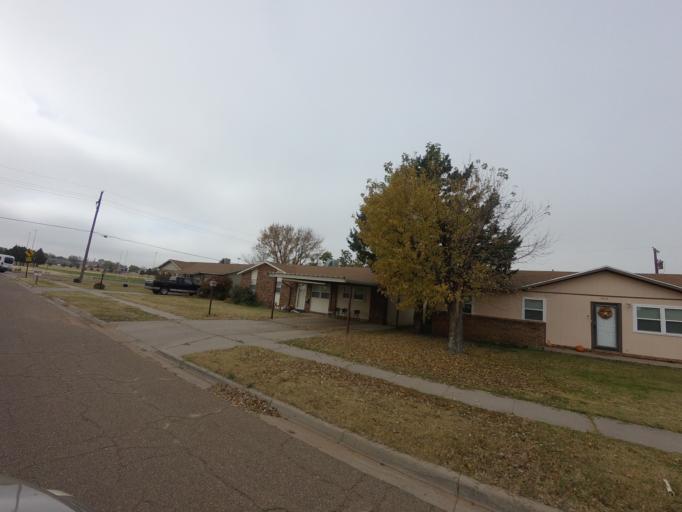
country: US
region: New Mexico
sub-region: Curry County
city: Clovis
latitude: 34.4270
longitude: -103.2279
